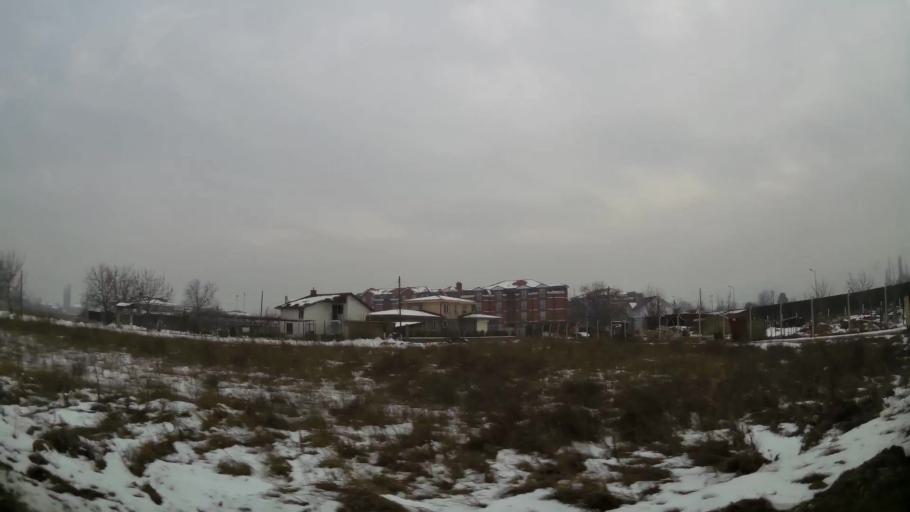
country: MK
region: Cucer-Sandevo
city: Chucher - Sandevo
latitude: 42.0508
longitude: 21.3650
